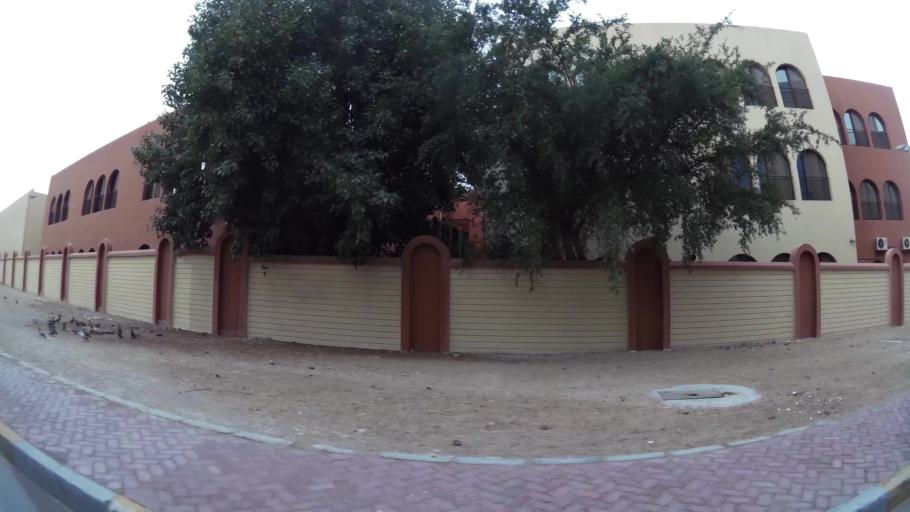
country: AE
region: Abu Dhabi
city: Abu Dhabi
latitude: 24.4688
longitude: 54.3788
